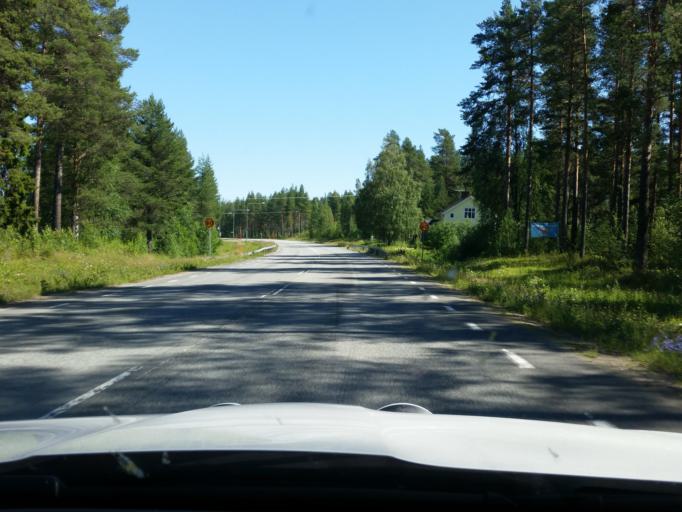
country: SE
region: Norrbotten
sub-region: Alvsbyns Kommun
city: AElvsbyn
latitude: 65.6661
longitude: 20.9779
